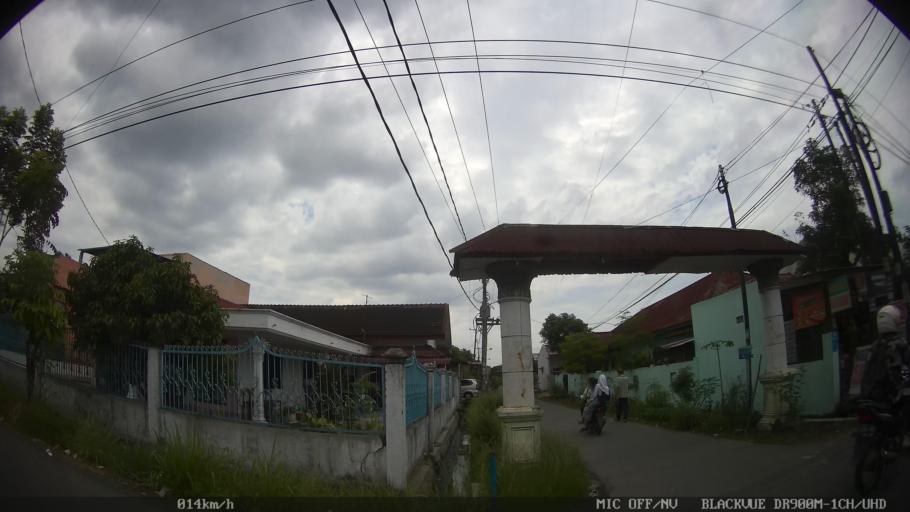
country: ID
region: North Sumatra
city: Sunggal
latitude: 3.5992
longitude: 98.6175
